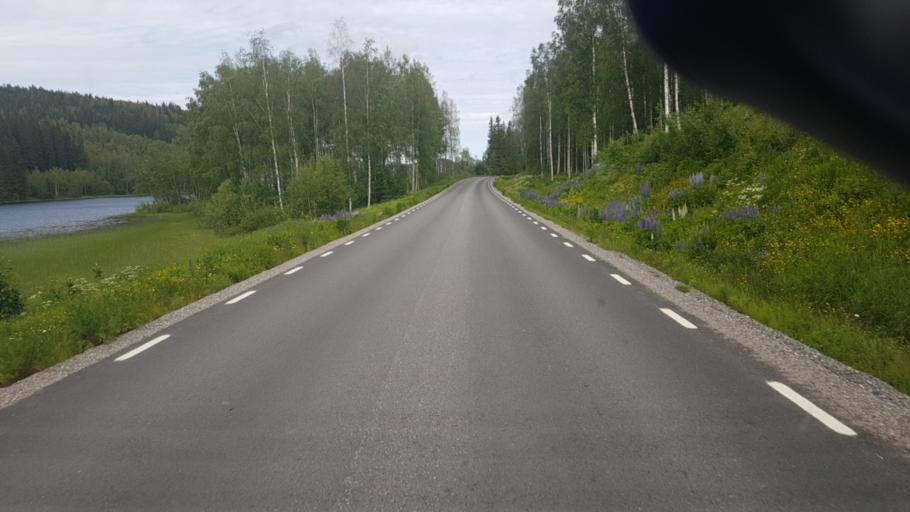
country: SE
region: Vaermland
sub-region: Eda Kommun
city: Amotfors
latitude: 59.8923
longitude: 12.5257
